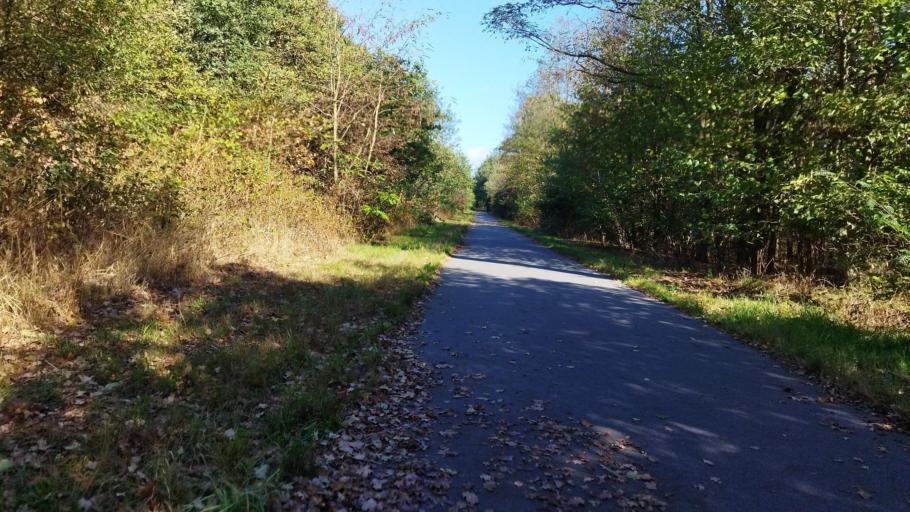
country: DE
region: Lower Saxony
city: Ohne
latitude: 52.2677
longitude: 7.3142
